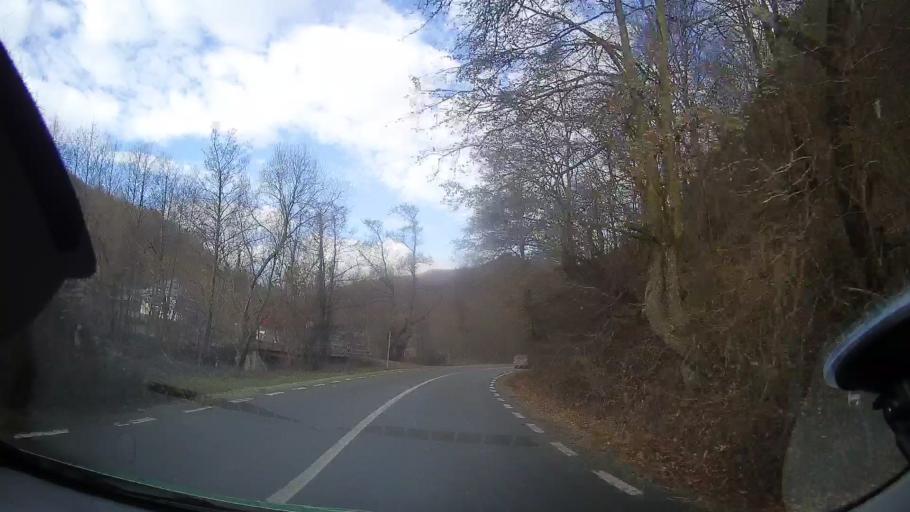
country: RO
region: Cluj
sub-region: Comuna Baisoara
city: Baisoara
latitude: 46.6028
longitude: 23.4249
